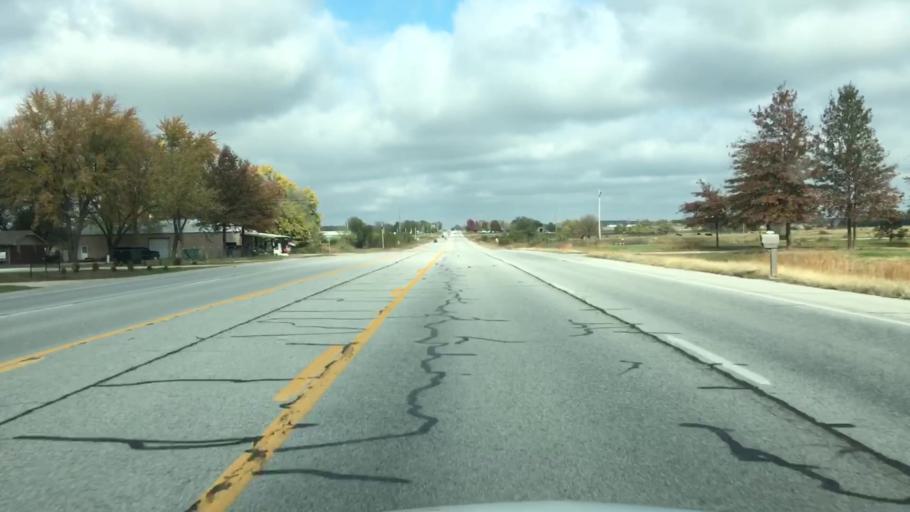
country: US
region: Arkansas
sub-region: Benton County
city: Siloam Springs
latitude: 36.2083
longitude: -94.4957
